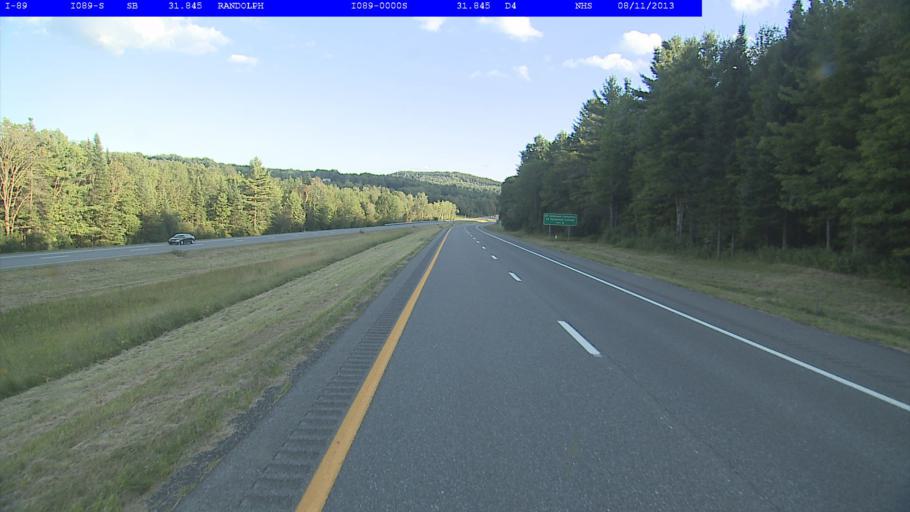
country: US
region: Vermont
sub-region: Orange County
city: Randolph
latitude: 43.9588
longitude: -72.6232
